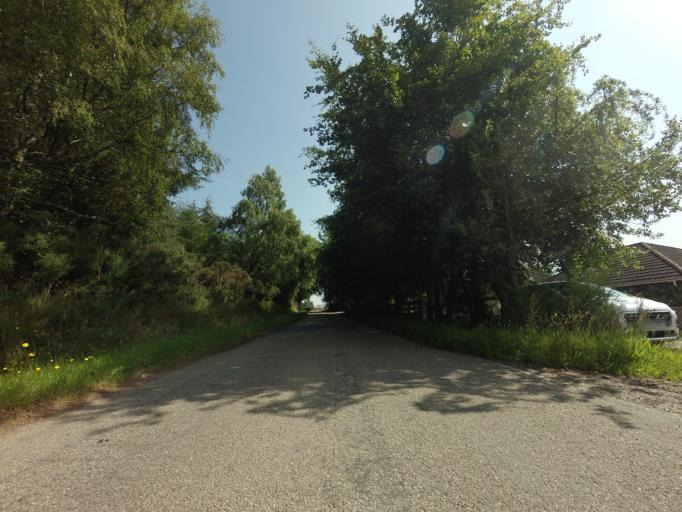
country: GB
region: Scotland
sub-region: Highland
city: Tain
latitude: 57.7595
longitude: -4.1209
